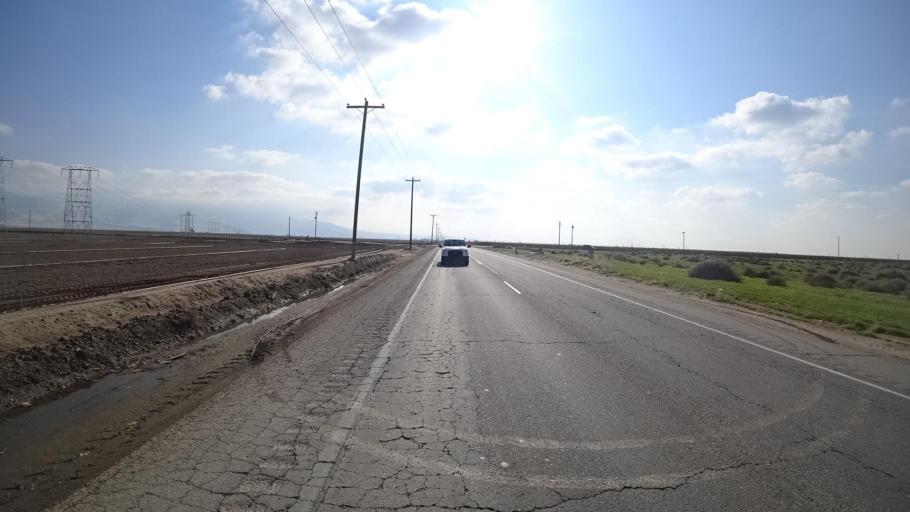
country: US
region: California
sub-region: Kern County
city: Arvin
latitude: 35.2539
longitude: -118.8248
